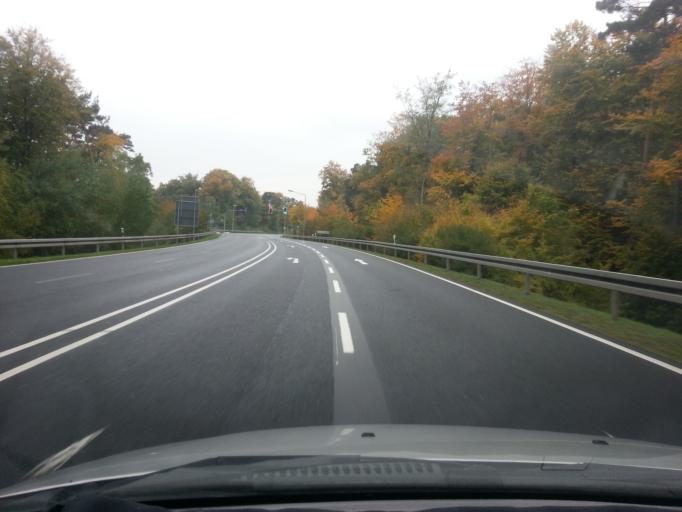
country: DE
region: Hesse
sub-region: Regierungsbezirk Darmstadt
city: Neu Isenburg
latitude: 50.0353
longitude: 8.7035
